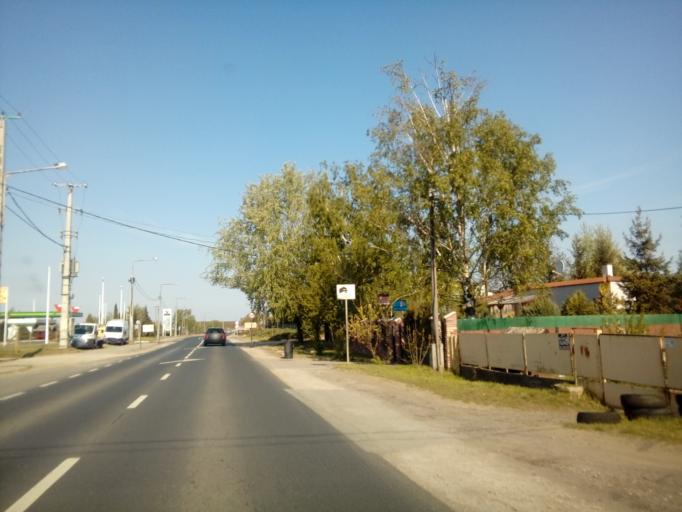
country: HU
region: Szabolcs-Szatmar-Bereg
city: Nagykallo
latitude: 47.8816
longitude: 21.8263
